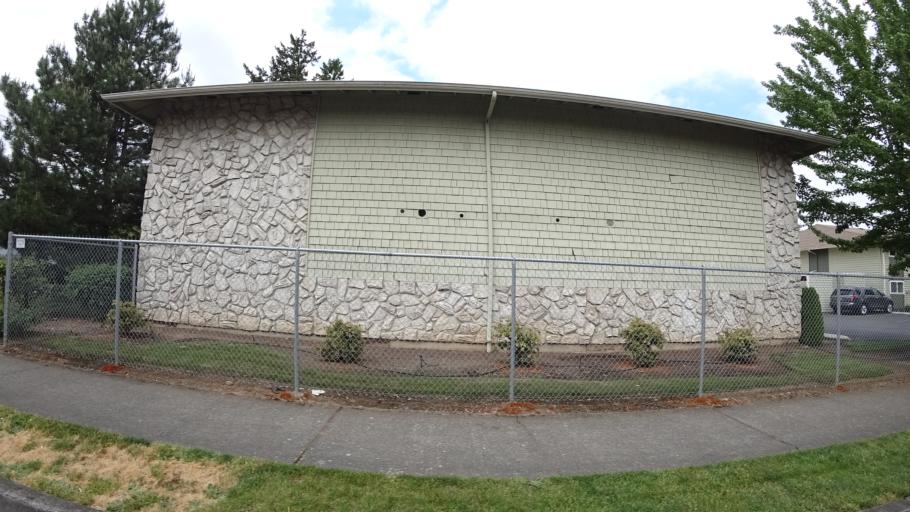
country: US
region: Oregon
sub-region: Multnomah County
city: Fairview
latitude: 45.5178
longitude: -122.4843
